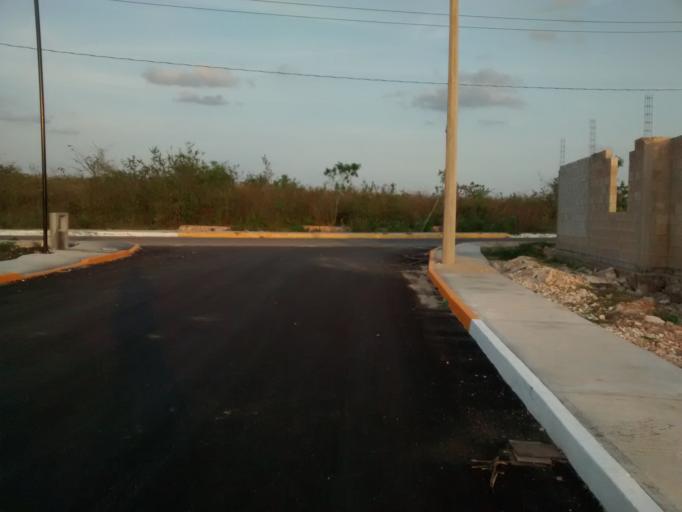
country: MX
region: Yucatan
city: Valladolid
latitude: 20.6810
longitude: -88.1922
